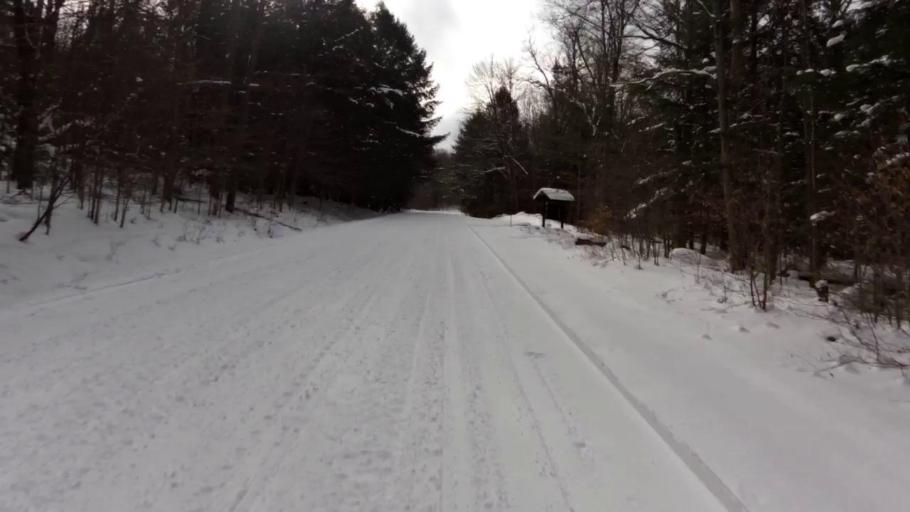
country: US
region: New York
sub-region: Cattaraugus County
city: Salamanca
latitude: 42.0802
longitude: -78.7494
